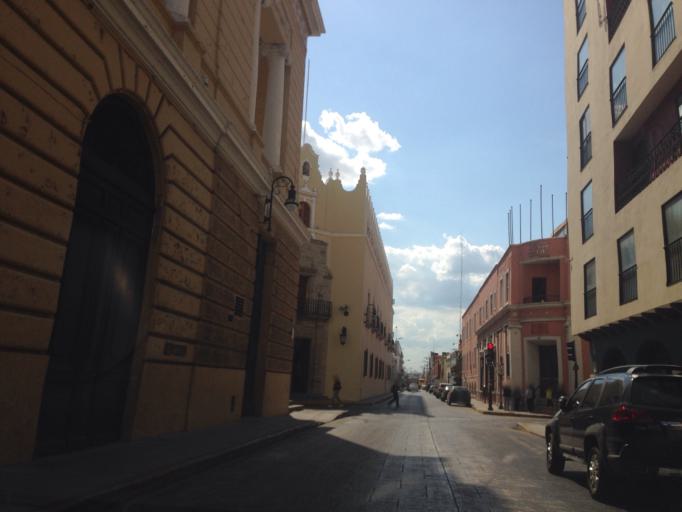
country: MX
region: Yucatan
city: Merida
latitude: 20.9697
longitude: -89.6222
